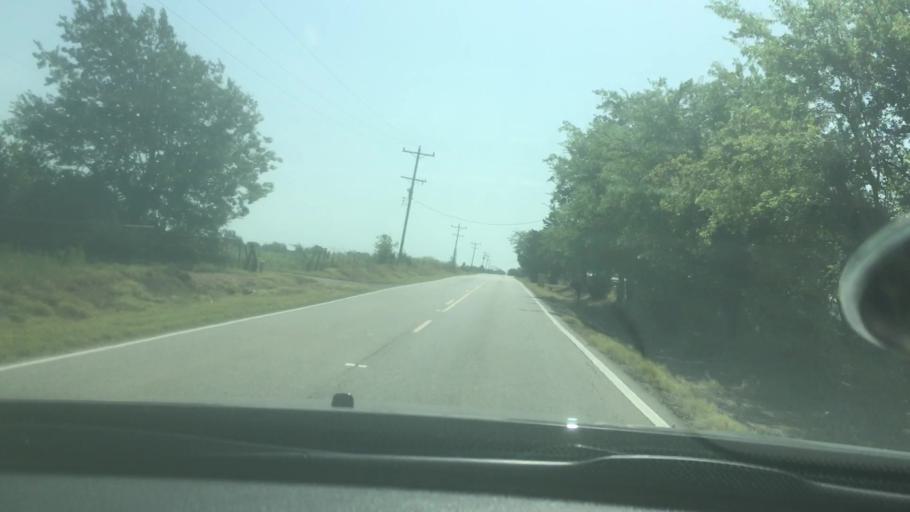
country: US
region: Oklahoma
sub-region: Bryan County
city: Durant
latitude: 34.0848
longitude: -96.4389
